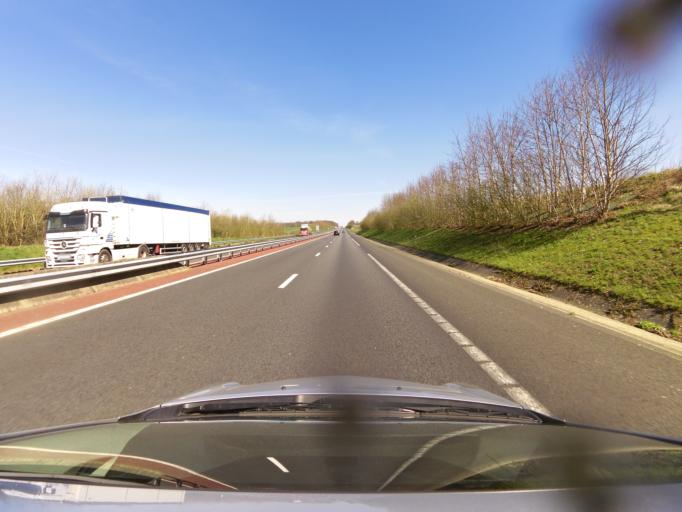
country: FR
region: Lower Normandy
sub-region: Departement de la Manche
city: Saint-Senier-sous-Avranches
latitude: 48.7548
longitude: -1.2788
